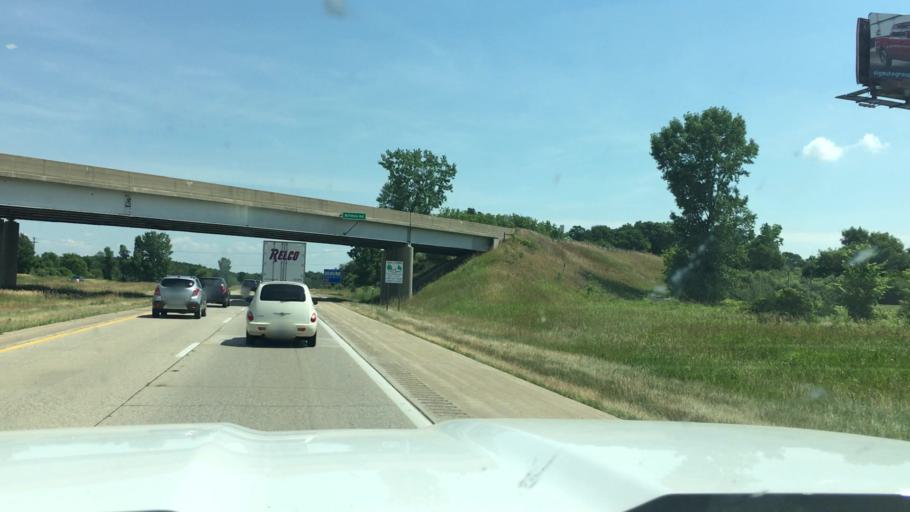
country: US
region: Michigan
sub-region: Shiawassee County
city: Perry
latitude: 42.8336
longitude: -84.2394
